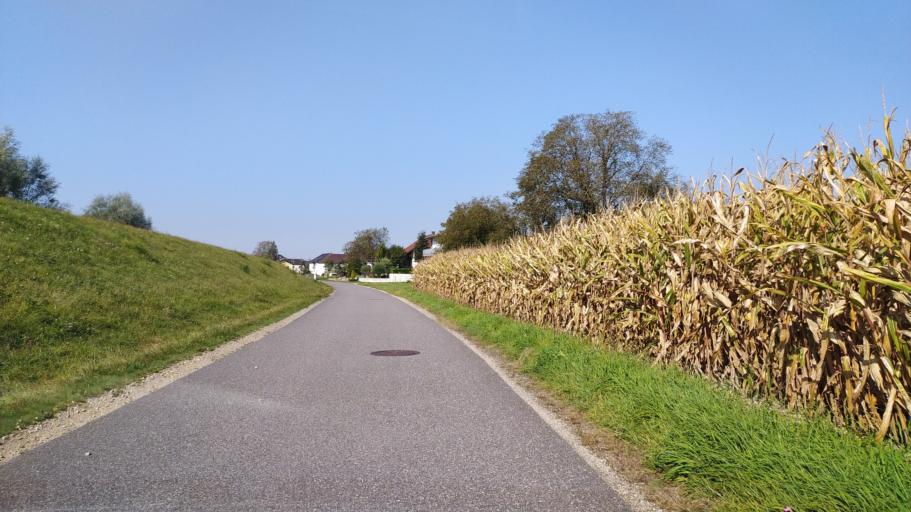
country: AT
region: Upper Austria
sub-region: Politischer Bezirk Perg
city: Perg
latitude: 48.1930
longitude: 14.7095
